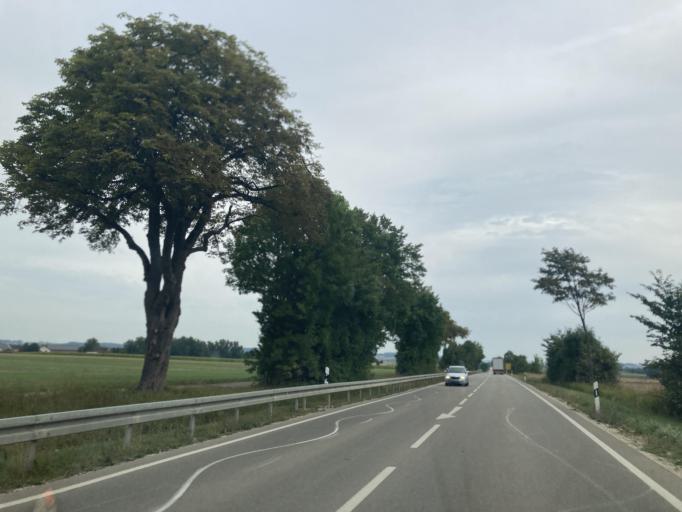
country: DE
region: Bavaria
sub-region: Swabia
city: Munningen
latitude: 48.9237
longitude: 10.5764
